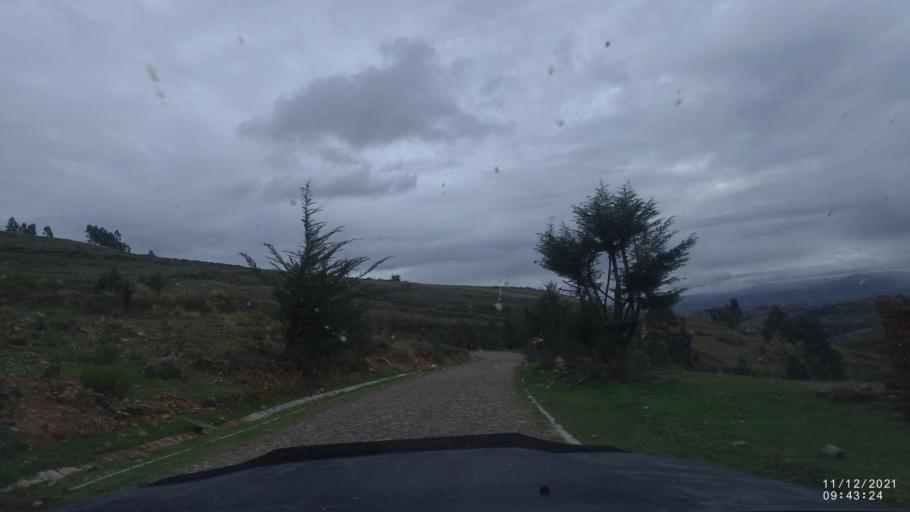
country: BO
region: Cochabamba
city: Tarata
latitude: -17.8012
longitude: -65.9778
